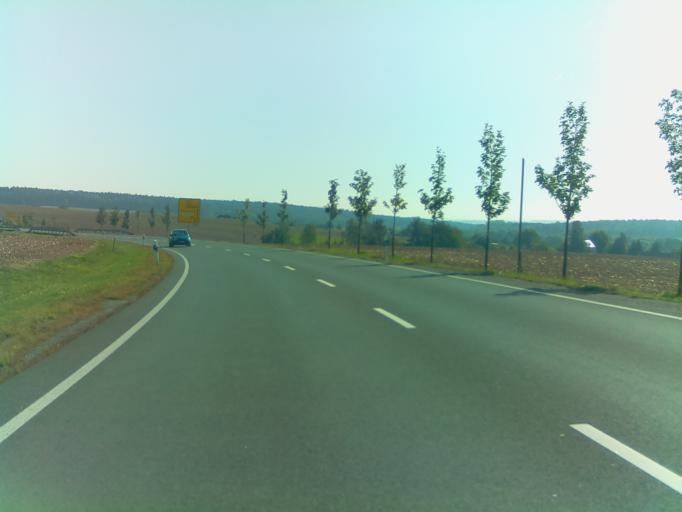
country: DE
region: Thuringia
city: Tautendorf
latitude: 50.8052
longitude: 11.9050
